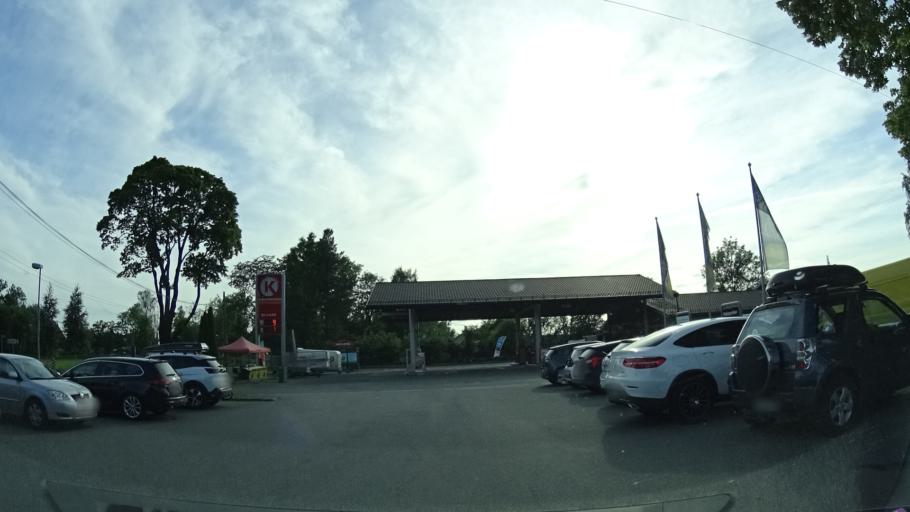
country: NO
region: Akershus
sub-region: Baerum
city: Lysaker
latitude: 59.9624
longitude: 10.6427
